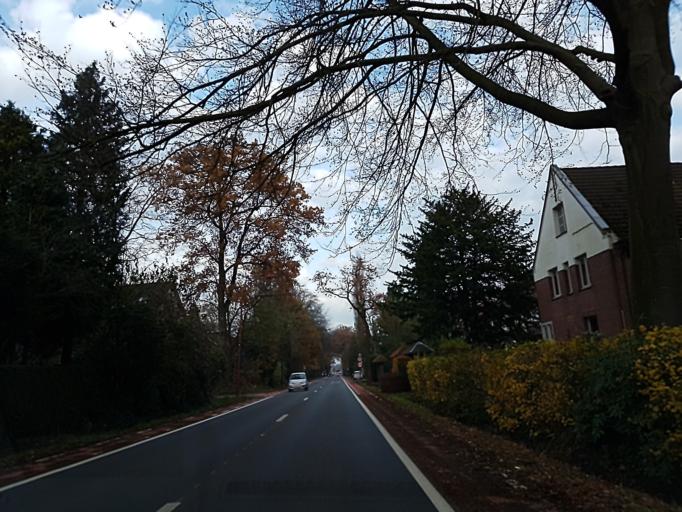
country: BE
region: Flanders
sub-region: Provincie Antwerpen
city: Kalmthout
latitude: 51.3692
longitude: 4.4690
